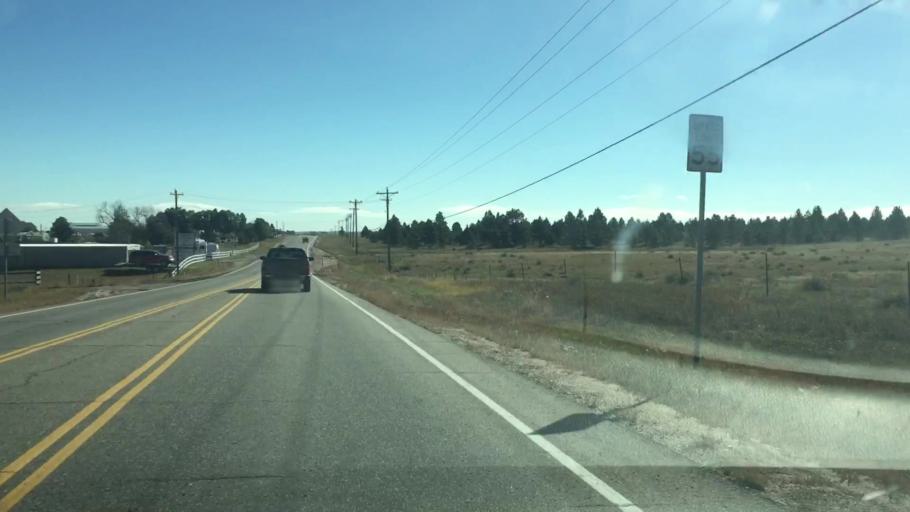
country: US
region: Colorado
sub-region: Elbert County
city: Elizabeth
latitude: 39.3613
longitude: -104.5688
